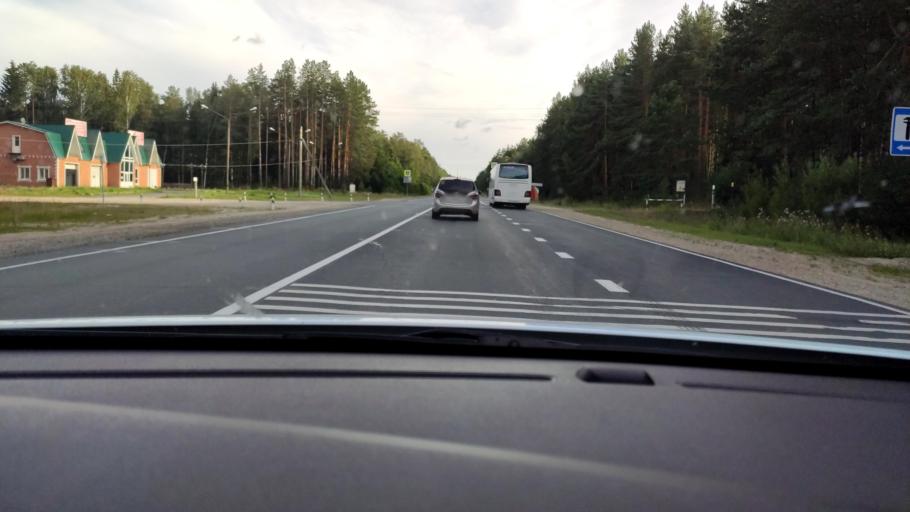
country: RU
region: Mariy-El
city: Suslonger
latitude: 56.3113
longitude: 48.2347
